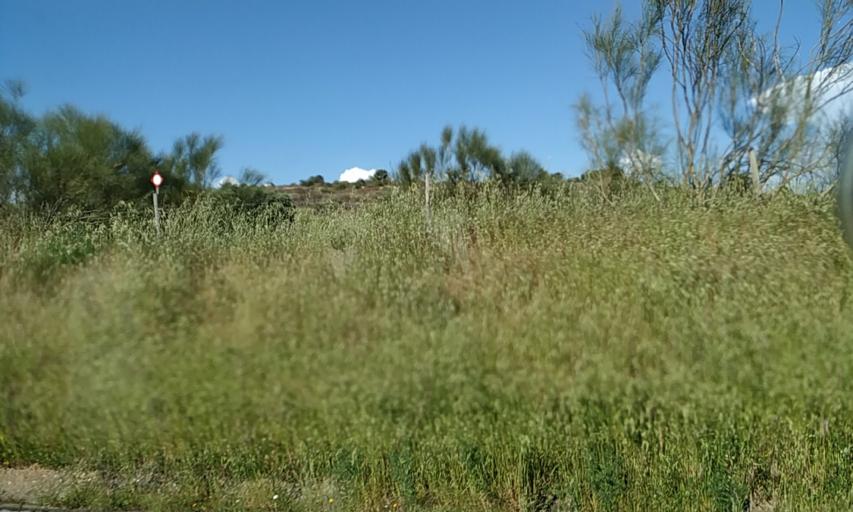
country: PT
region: Portalegre
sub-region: Portalegre
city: Urra
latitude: 39.0802
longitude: -7.4368
